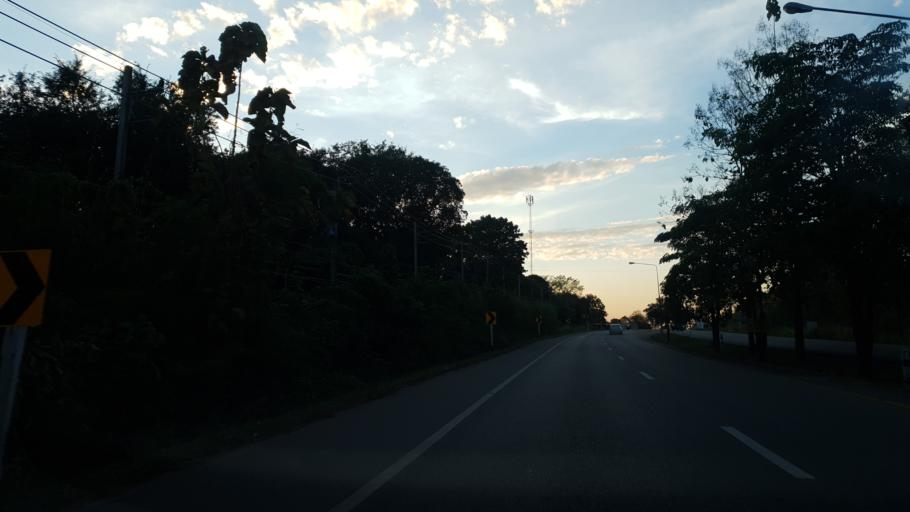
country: TH
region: Phitsanulok
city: Nakhon Thai
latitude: 16.8570
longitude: 100.7357
